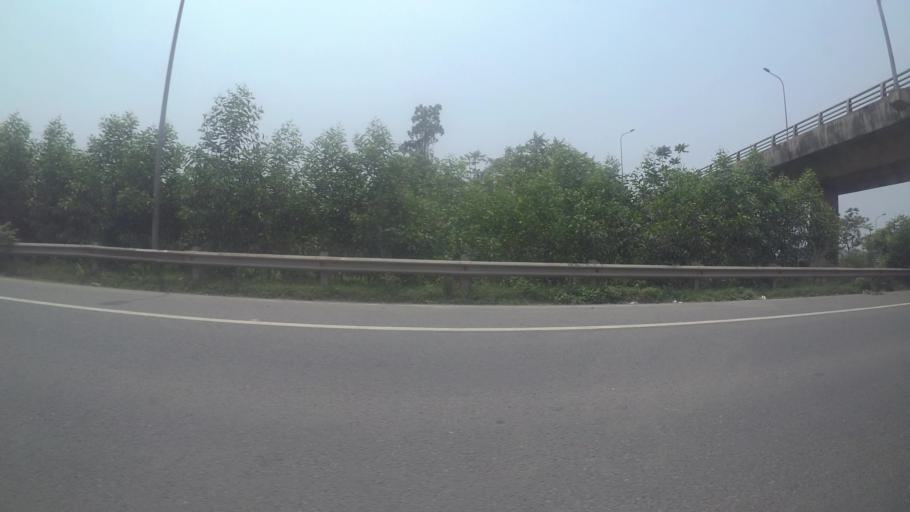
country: VN
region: Ha Noi
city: Quoc Oai
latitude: 20.9890
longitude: 105.5753
